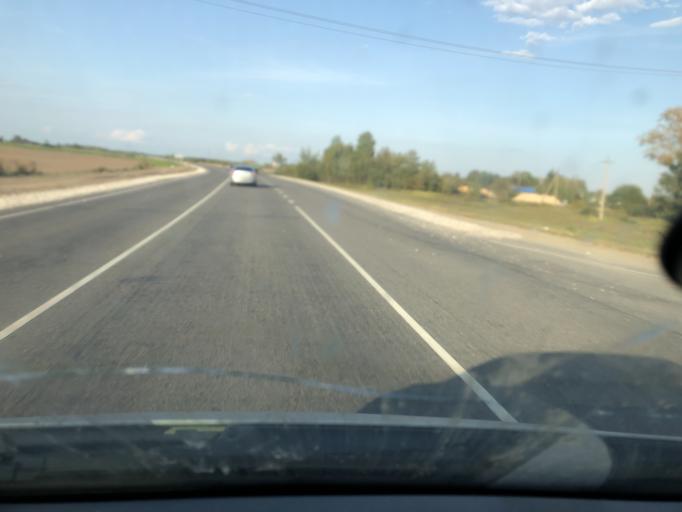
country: RU
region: Kaluga
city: Peremyshl'
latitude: 54.2547
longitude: 36.1235
